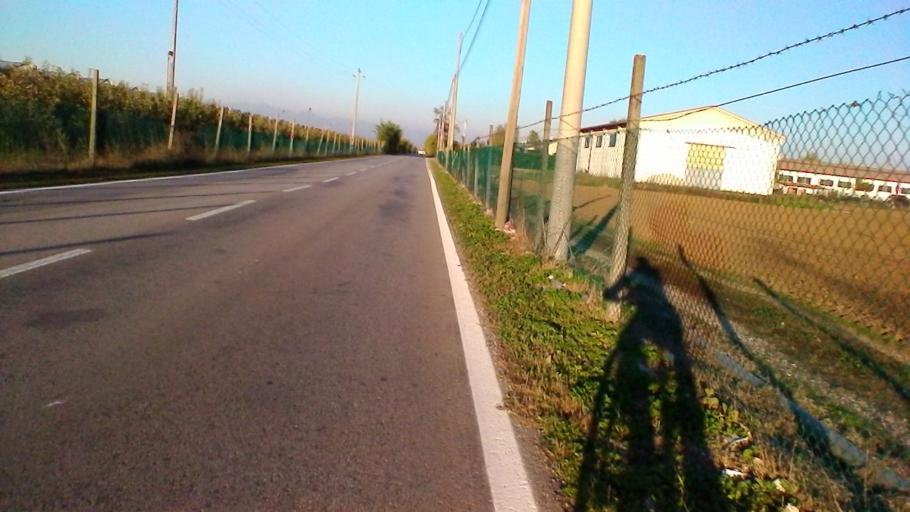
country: IT
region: Veneto
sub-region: Provincia di Verona
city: Alpo
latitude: 45.3590
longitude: 10.9030
